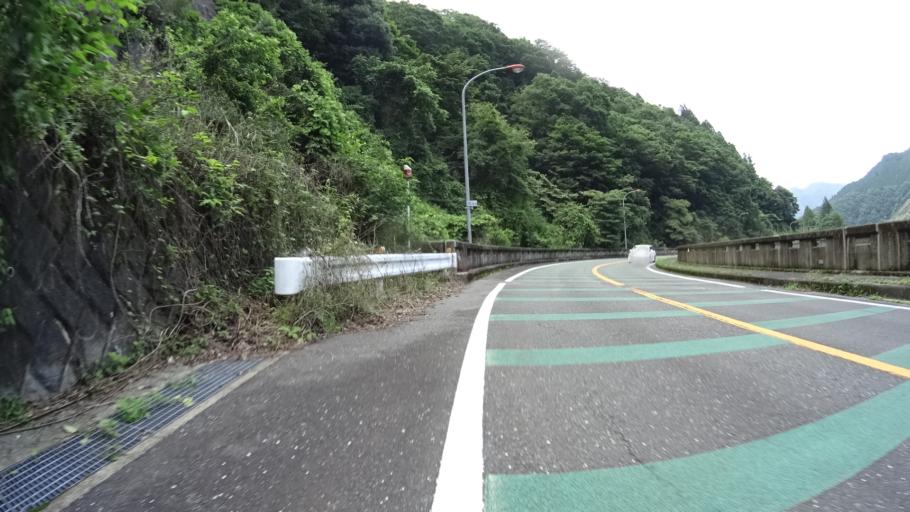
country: JP
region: Kanagawa
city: Hadano
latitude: 35.5047
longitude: 139.2294
